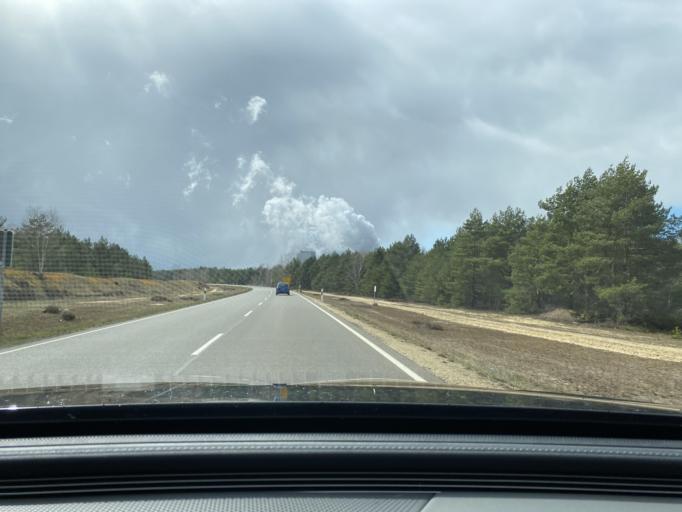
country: DE
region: Saxony
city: Boxberg
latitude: 51.4243
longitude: 14.6107
